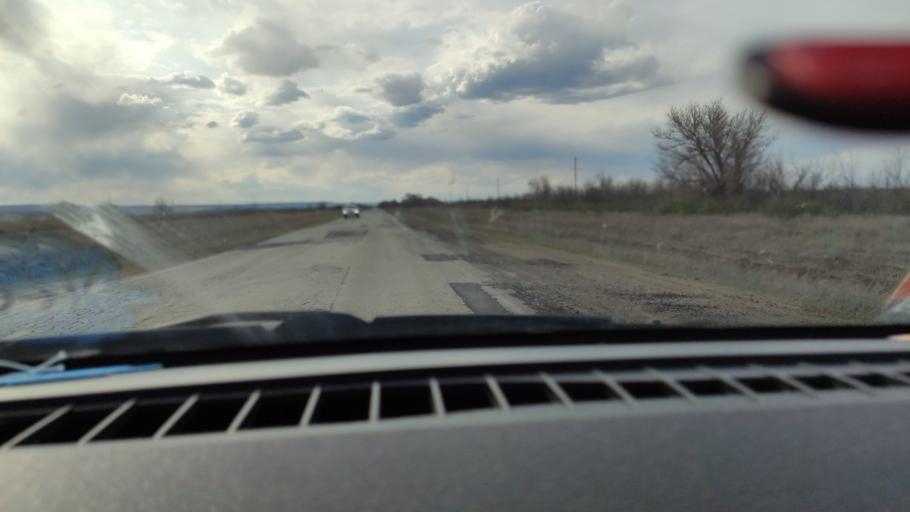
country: RU
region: Saratov
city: Rovnoye
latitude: 51.0652
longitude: 46.0089
